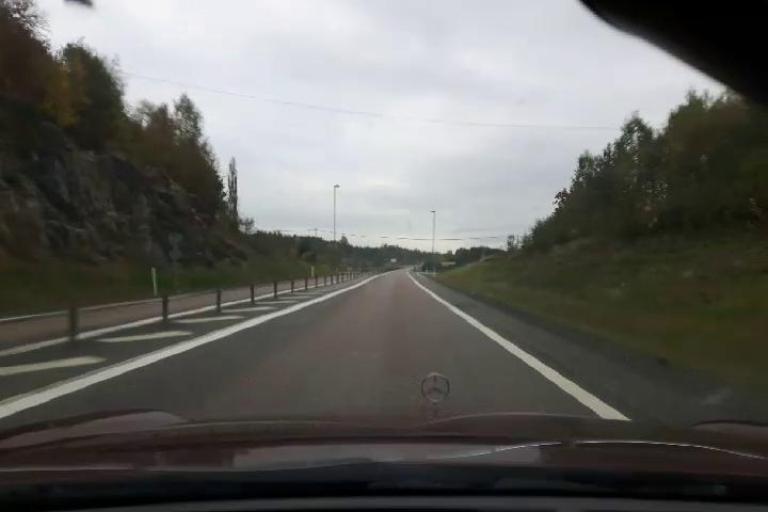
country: SE
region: Vaesternorrland
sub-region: Kramfors Kommun
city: Nordingra
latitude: 62.9234
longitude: 18.0992
